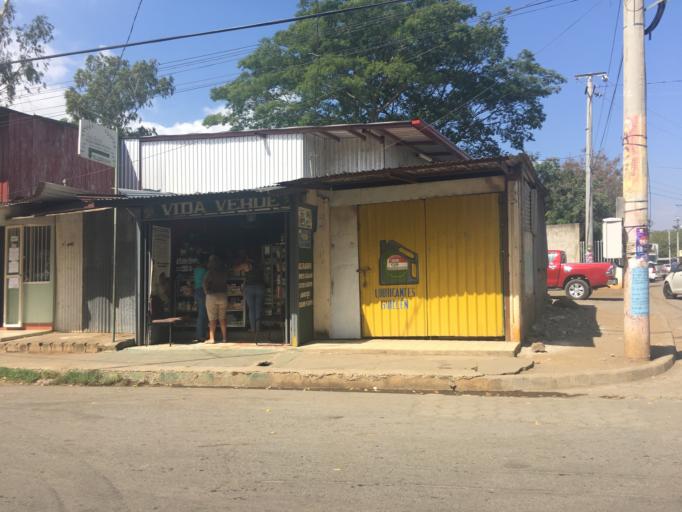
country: NI
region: Managua
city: Ciudad Sandino
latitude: 12.1643
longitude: -86.3575
